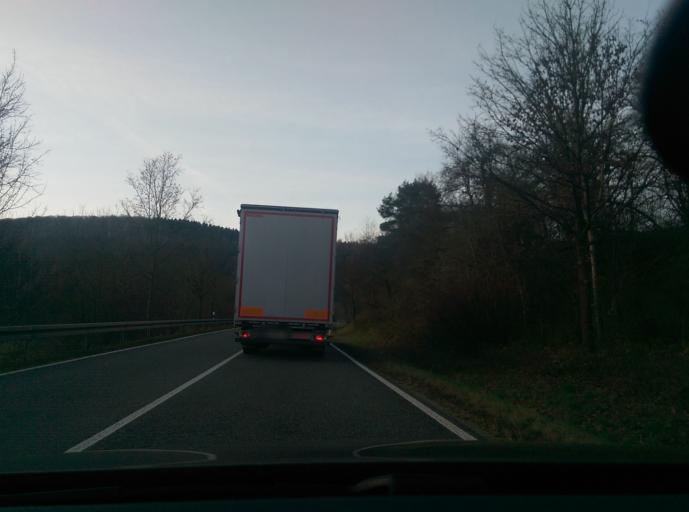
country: DE
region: Hesse
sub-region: Regierungsbezirk Kassel
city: Sontra
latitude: 51.0733
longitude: 9.9926
